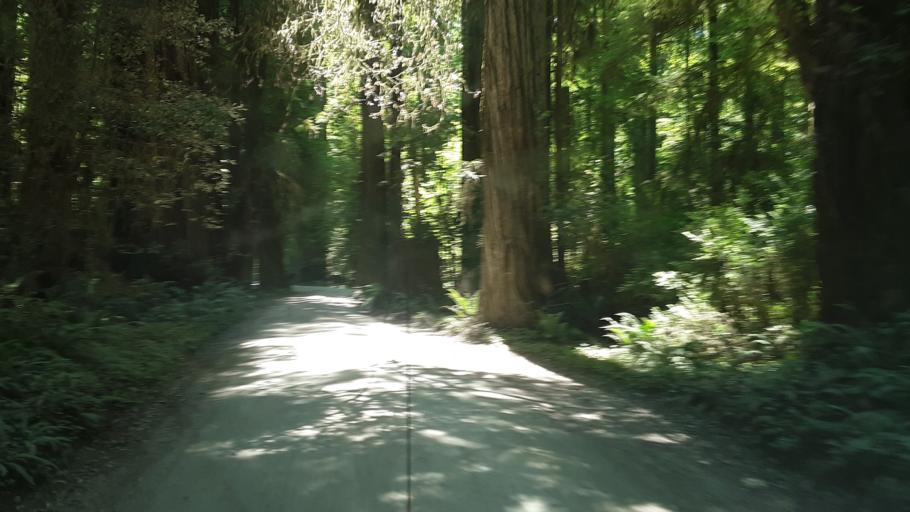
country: US
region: California
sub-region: Del Norte County
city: Bertsch-Oceanview
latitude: 41.8186
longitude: -124.1114
